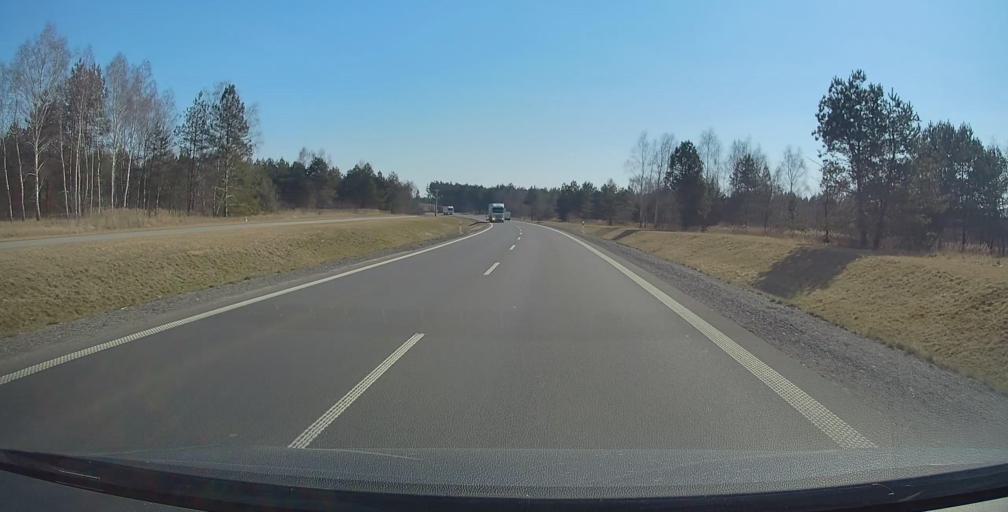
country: PL
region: Subcarpathian Voivodeship
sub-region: Powiat nizanski
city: Raclawice
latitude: 50.4976
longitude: 22.1793
